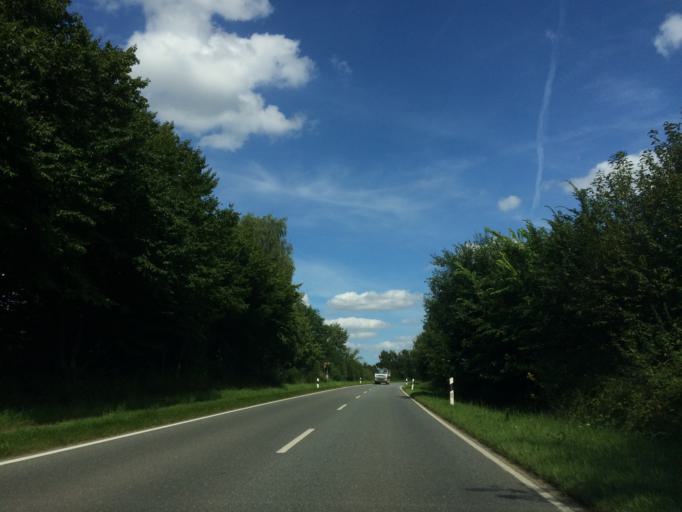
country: DE
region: Schleswig-Holstein
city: Bosdorf
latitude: 54.1457
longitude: 10.4860
